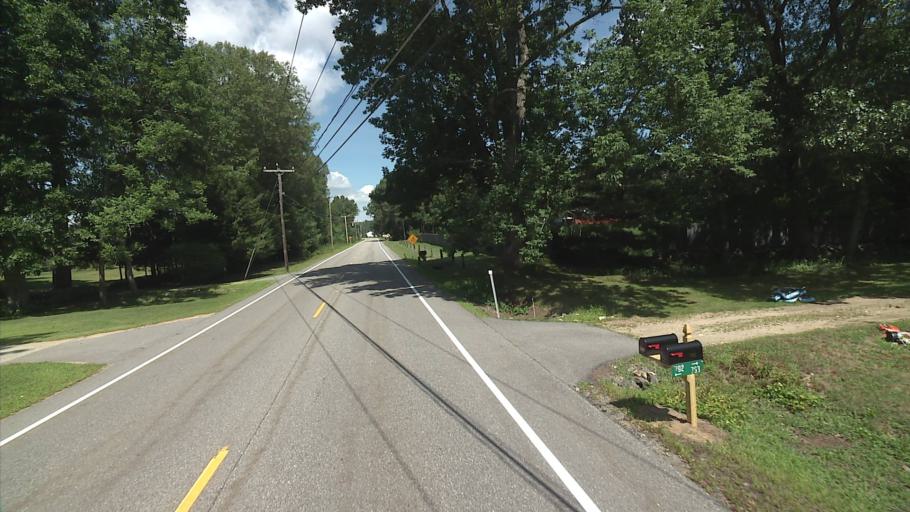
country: US
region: Massachusetts
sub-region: Worcester County
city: Southbridge
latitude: 41.9656
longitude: -72.0801
